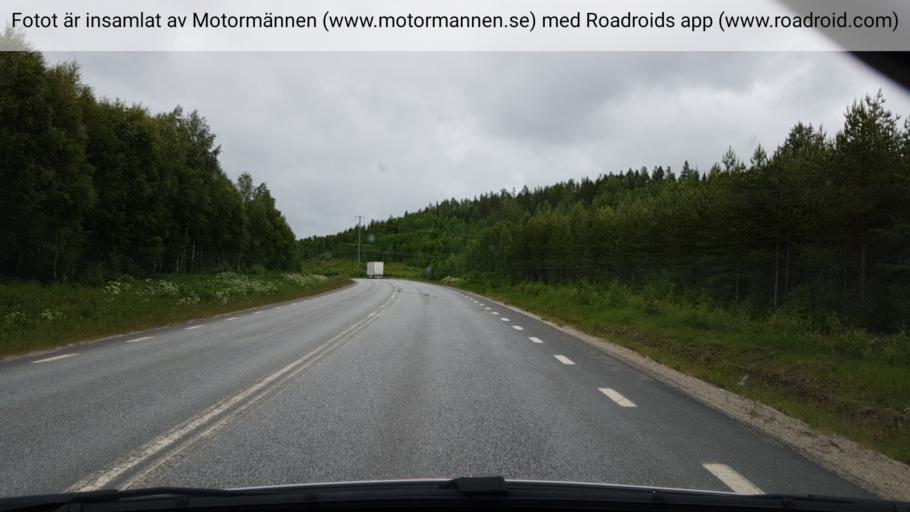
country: SE
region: Vaesterbotten
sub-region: Vannas Kommun
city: Vaennaes
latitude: 63.9896
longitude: 19.7316
